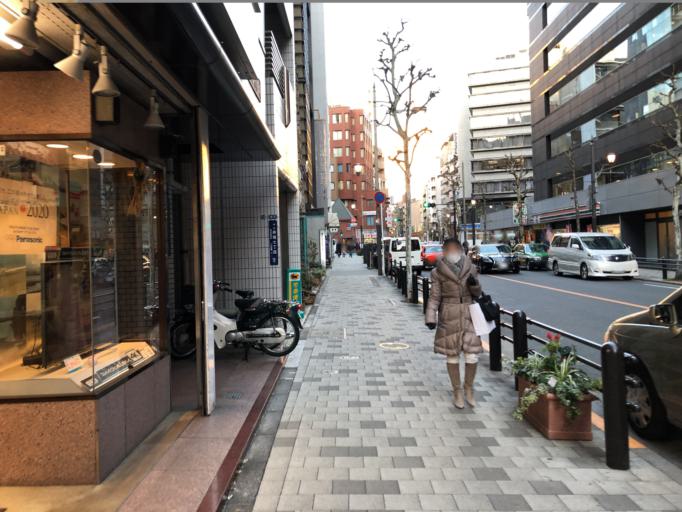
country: JP
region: Tokyo
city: Tokyo
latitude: 35.6696
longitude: 139.7329
